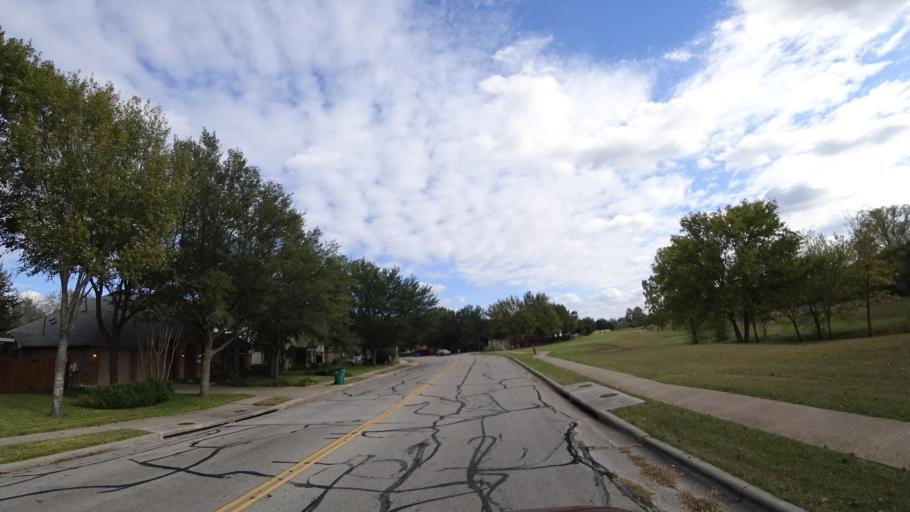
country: US
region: Texas
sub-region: Travis County
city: Pflugerville
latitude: 30.4342
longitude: -97.6255
